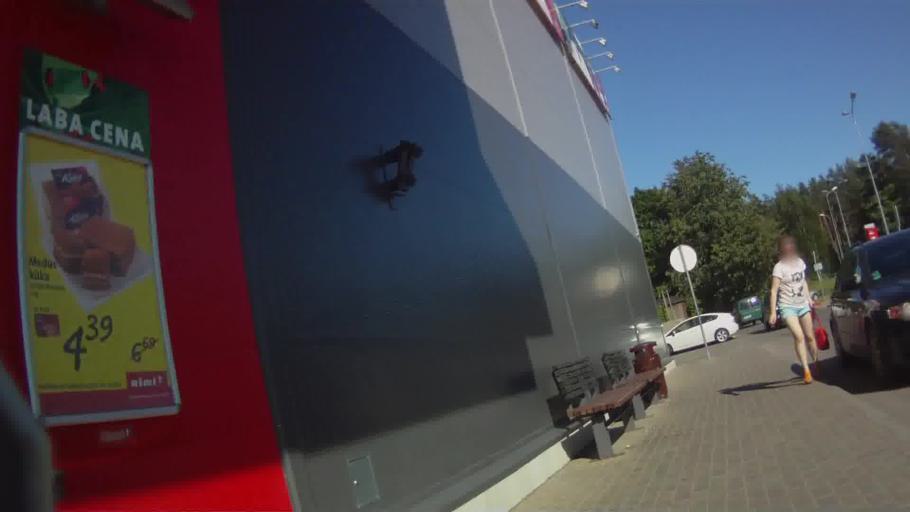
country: LV
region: Stopini
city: Ulbroka
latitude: 56.9567
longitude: 24.2543
